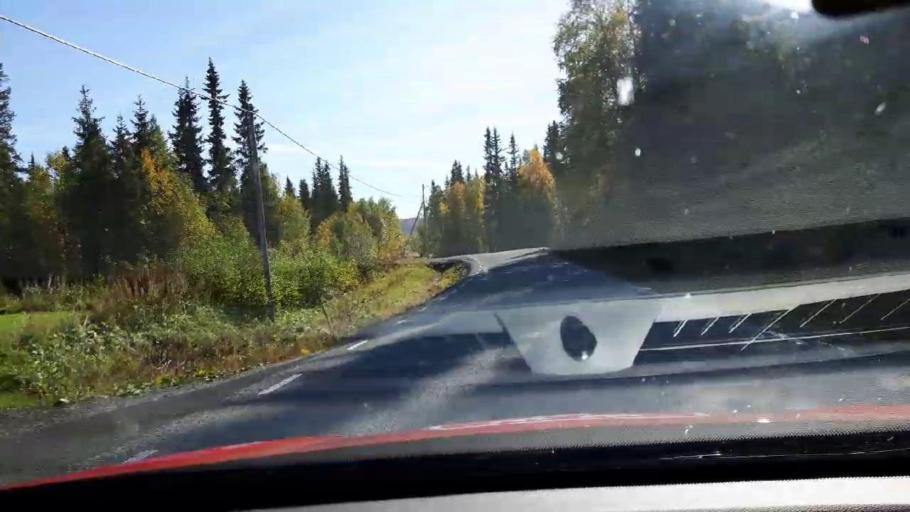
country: NO
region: Nord-Trondelag
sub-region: Royrvik
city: Royrvik
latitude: 64.8183
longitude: 14.1444
